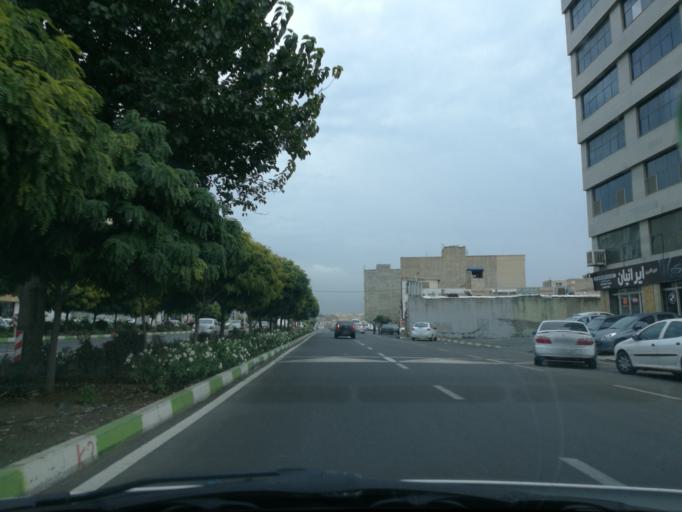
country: IR
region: Alborz
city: Karaj
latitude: 35.8528
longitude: 50.9622
